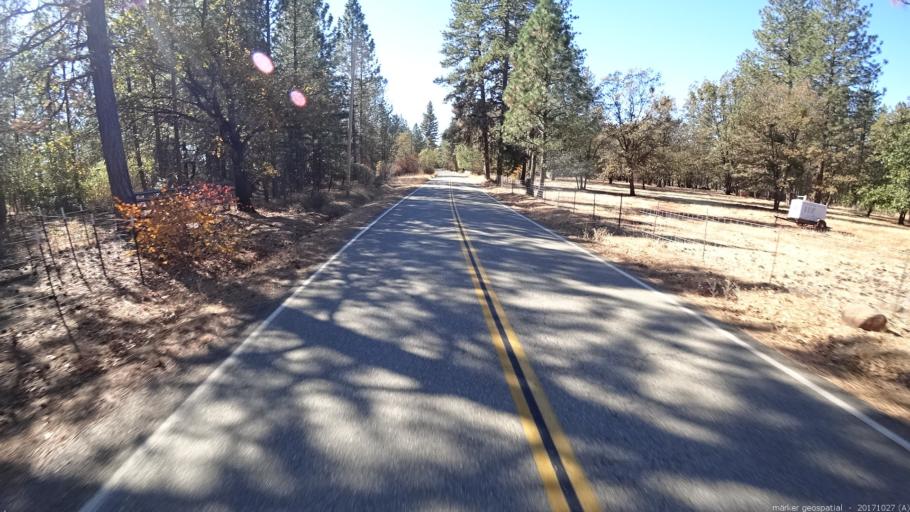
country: US
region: California
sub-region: Shasta County
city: Bella Vista
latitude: 40.6916
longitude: -122.0142
